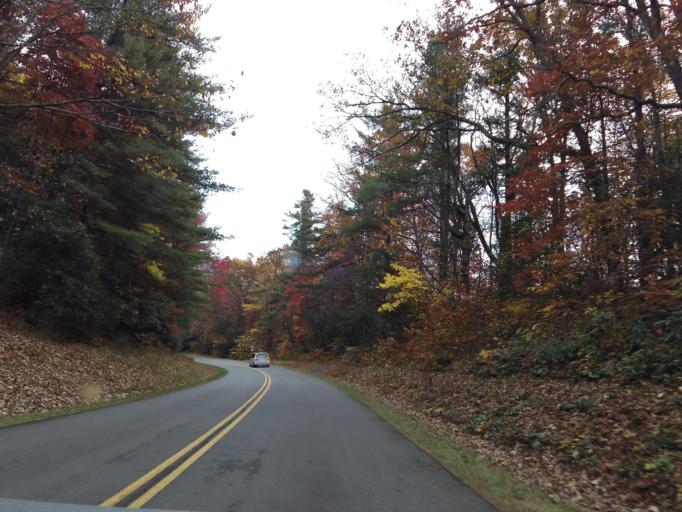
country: US
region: North Carolina
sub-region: Ashe County
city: Jefferson
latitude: 36.3169
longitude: -81.3674
